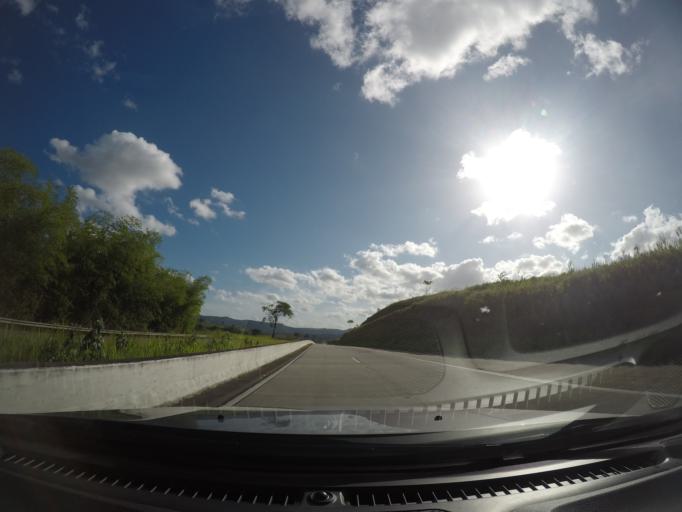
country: BR
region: Alagoas
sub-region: Flexeiras
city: Flexeiras
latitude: -9.1736
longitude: -35.7773
